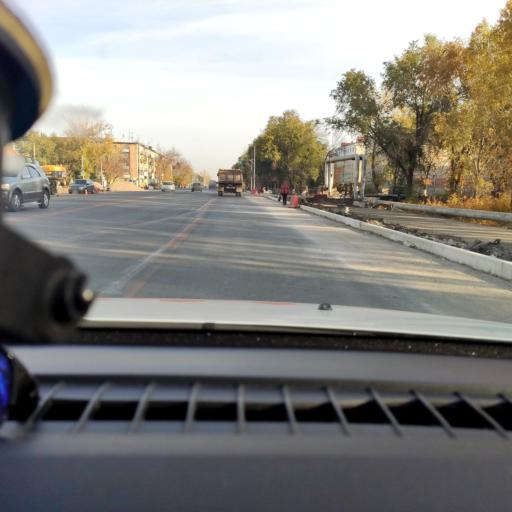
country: RU
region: Samara
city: Samara
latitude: 53.1171
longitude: 50.0854
